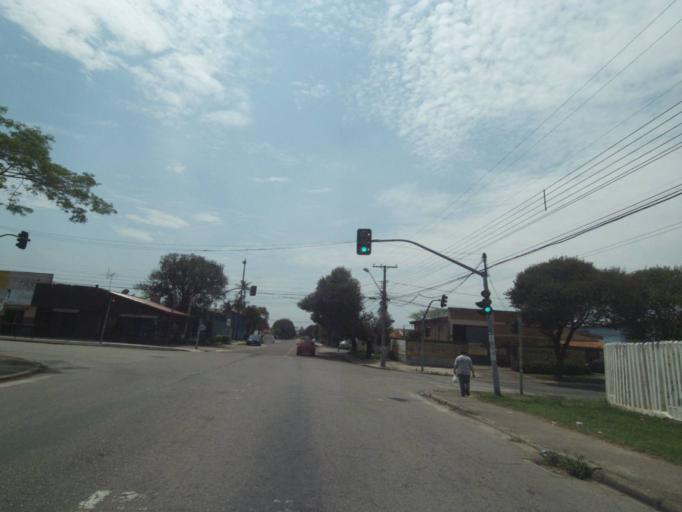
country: BR
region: Parana
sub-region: Pinhais
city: Pinhais
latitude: -25.4268
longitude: -49.2024
